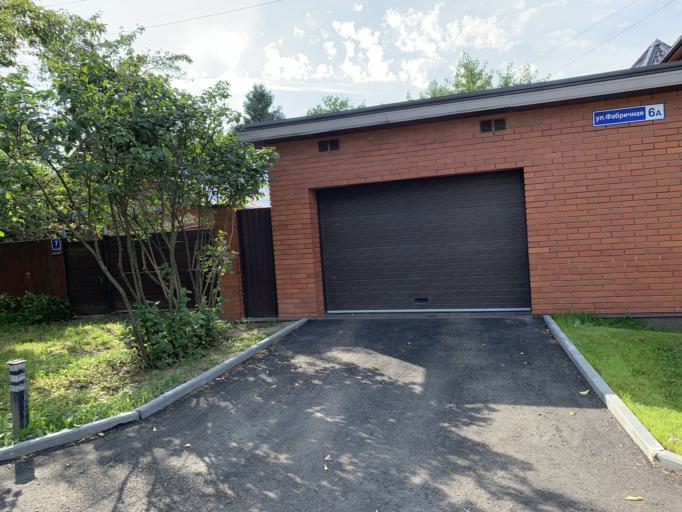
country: RU
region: Moskovskaya
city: Lesnyye Polyany
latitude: 55.9855
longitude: 37.8494
